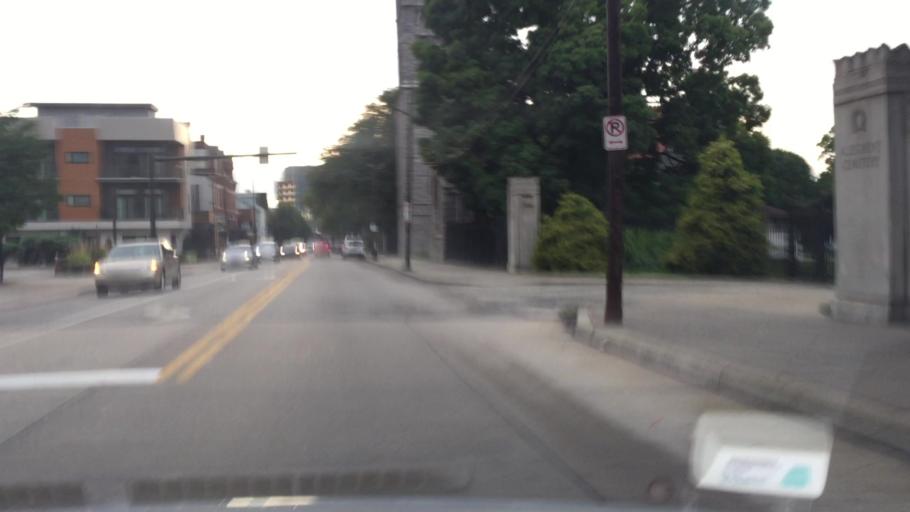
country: US
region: Pennsylvania
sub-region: Allegheny County
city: Bloomfield
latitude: 40.4656
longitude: -79.9466
